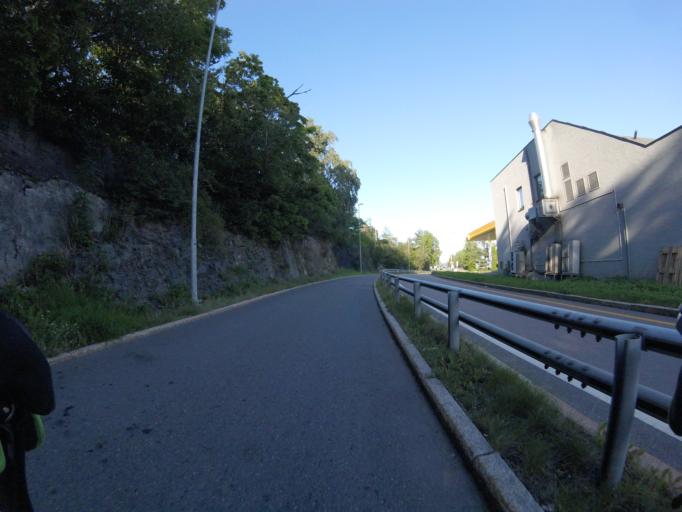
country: NO
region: Oslo
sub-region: Oslo
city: Oslo
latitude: 59.9442
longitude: 10.8327
